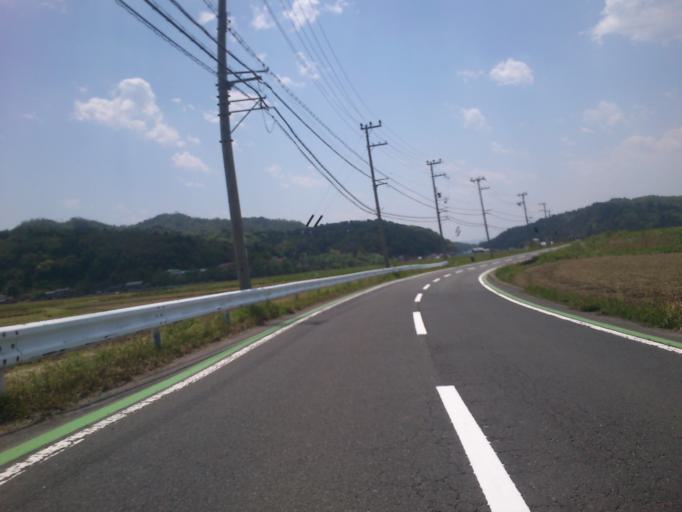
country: JP
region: Kyoto
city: Miyazu
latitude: 35.7184
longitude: 135.1083
